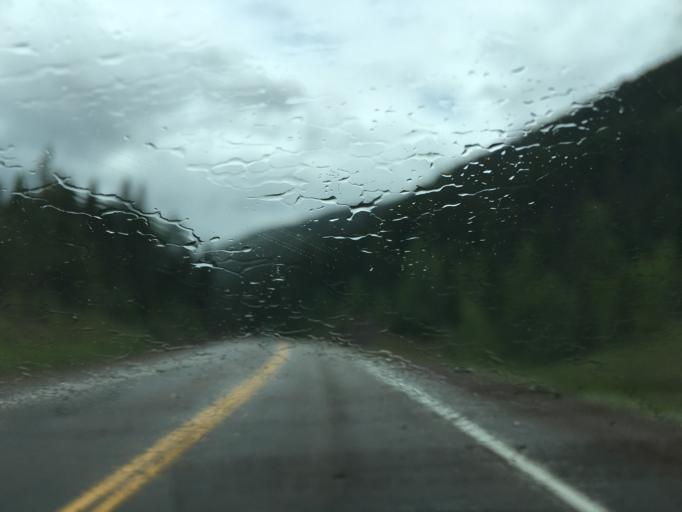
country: US
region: Montana
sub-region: Flathead County
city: Bigfork
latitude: 48.2441
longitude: -113.5656
